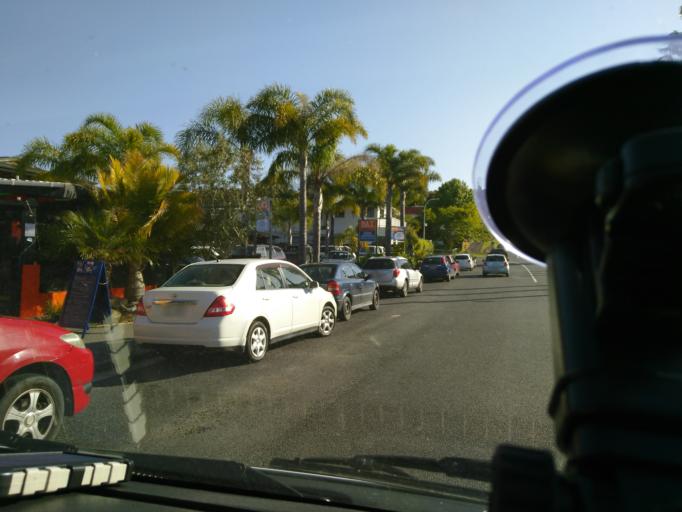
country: NZ
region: Northland
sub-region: Far North District
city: Paihia
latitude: -35.2857
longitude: 174.0947
